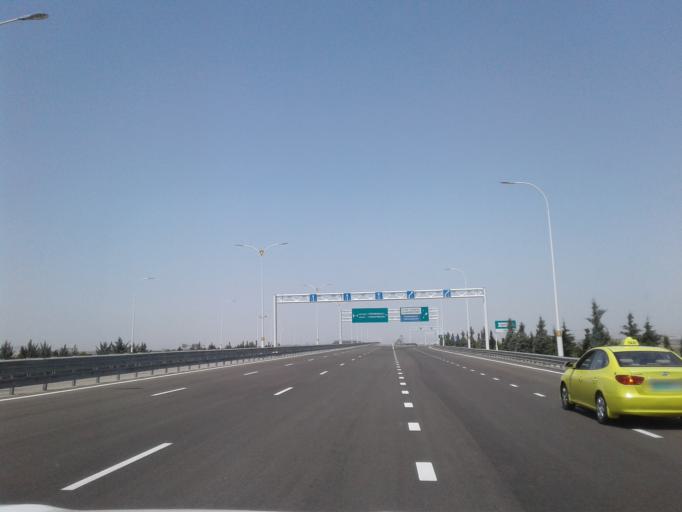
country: TM
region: Balkan
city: Turkmenbasy
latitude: 39.9760
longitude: 52.8683
